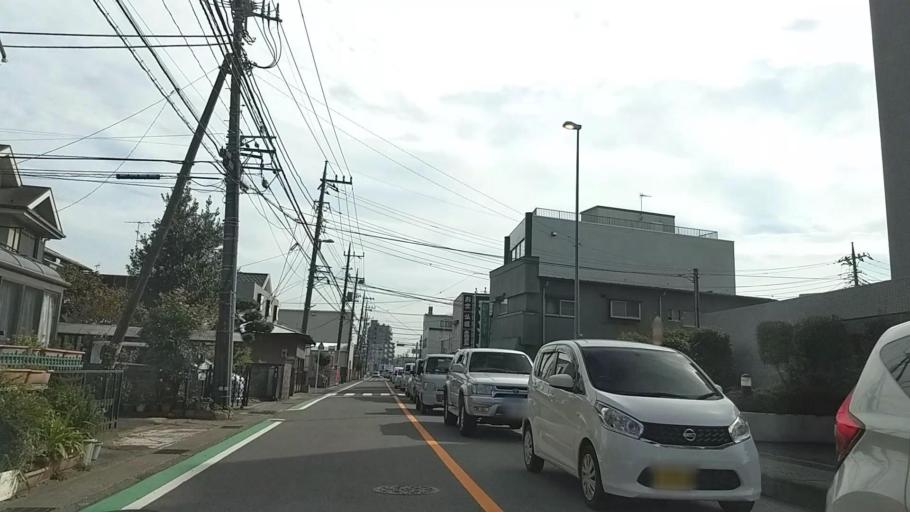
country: JP
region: Kanagawa
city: Atsugi
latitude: 35.4484
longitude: 139.3625
